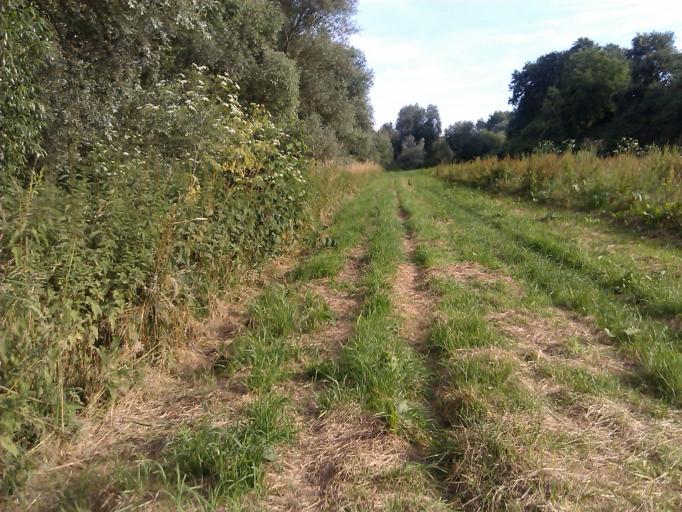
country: DE
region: Baden-Wuerttemberg
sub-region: Regierungsbezirk Stuttgart
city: Untereisesheim
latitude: 49.2056
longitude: 9.2126
